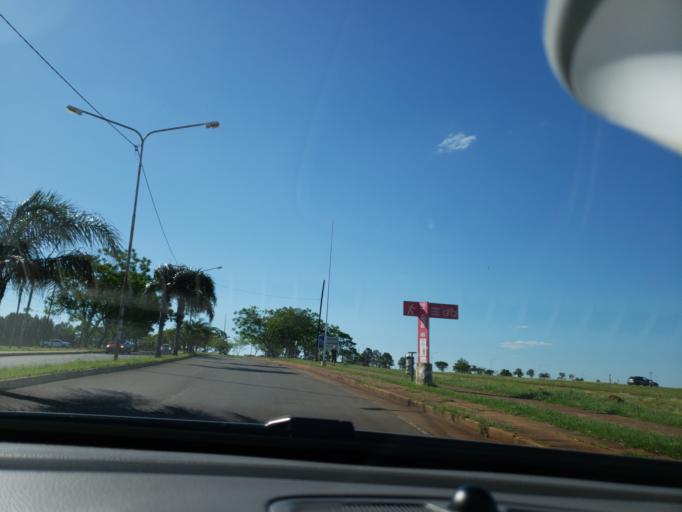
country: AR
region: Misiones
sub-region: Departamento de Capital
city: Posadas
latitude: -27.3945
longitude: -55.9616
